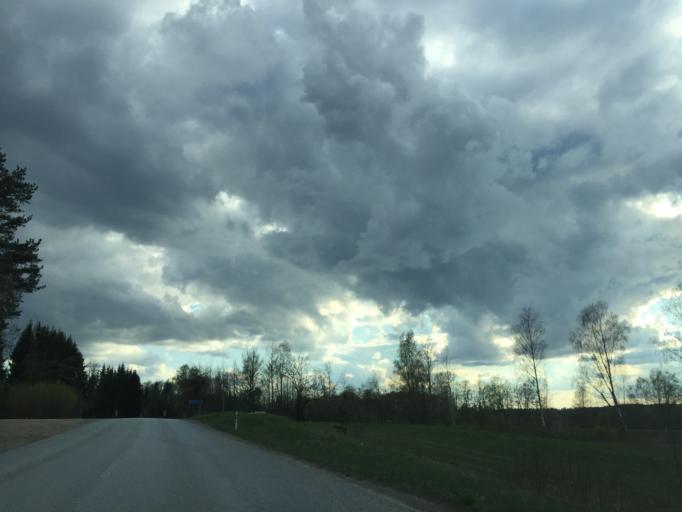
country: LV
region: Priekuli
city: Priekuli
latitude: 57.3462
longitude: 25.3439
